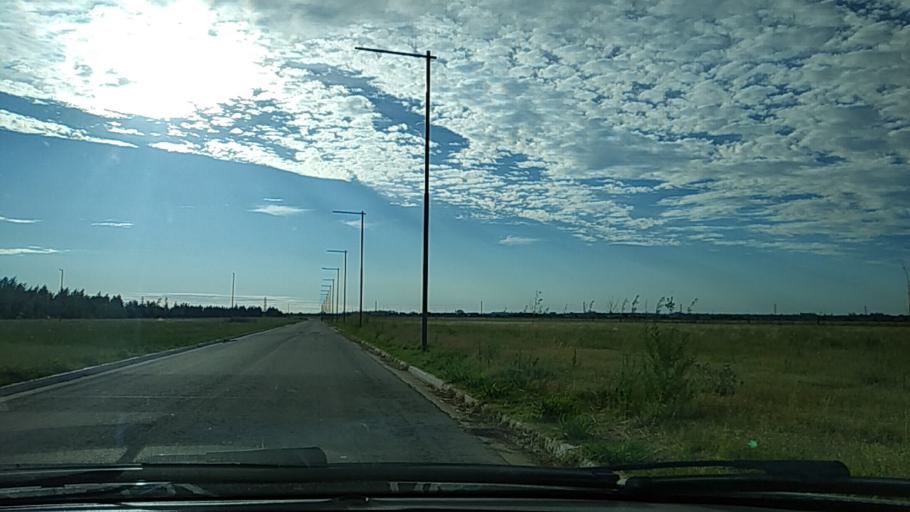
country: AR
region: Santa Fe
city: Funes
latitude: -32.9471
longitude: -60.7699
